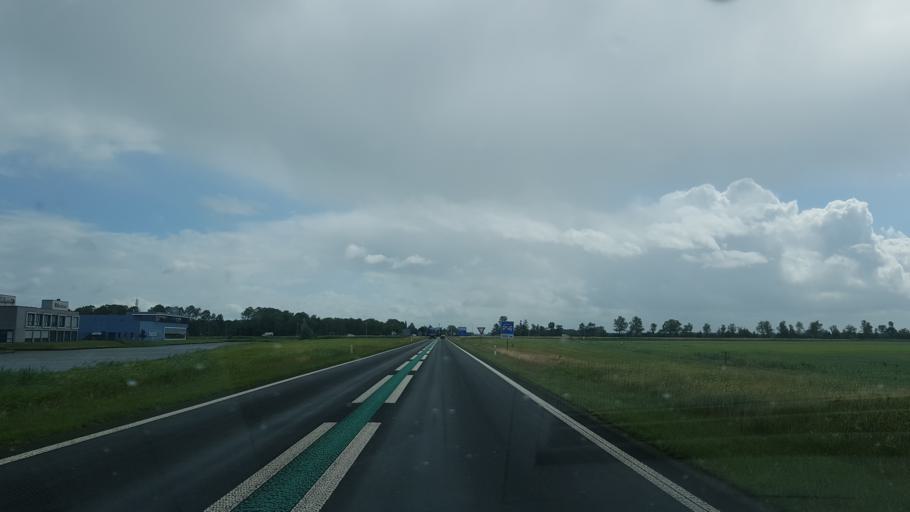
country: NL
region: Friesland
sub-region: Gemeente Dongeradeel
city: Dokkum
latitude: 53.3102
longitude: 5.9873
